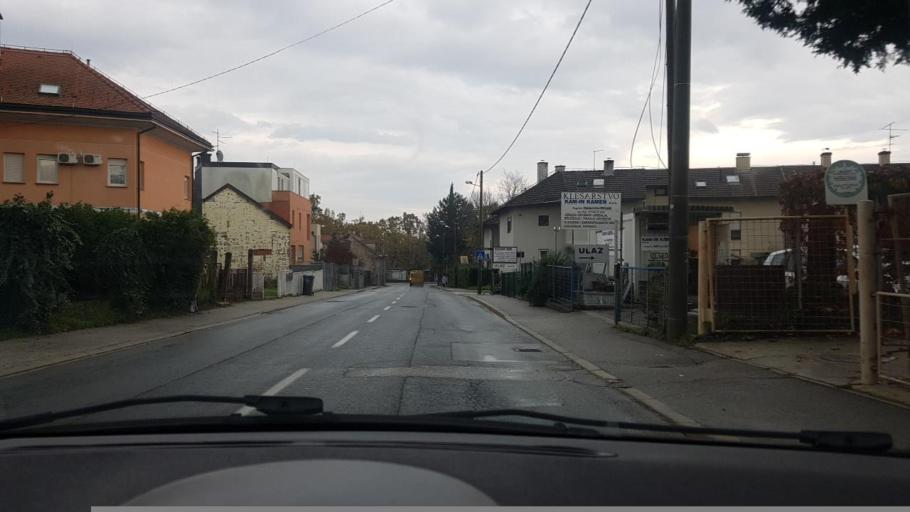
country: HR
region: Grad Zagreb
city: Zagreb
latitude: 45.8307
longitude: 15.9848
